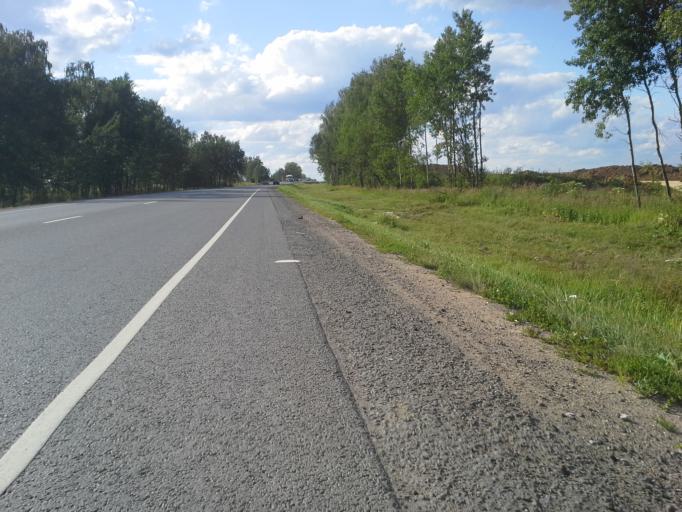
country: RU
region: Moskovskaya
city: L'vovskiy
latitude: 55.3525
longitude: 37.4441
